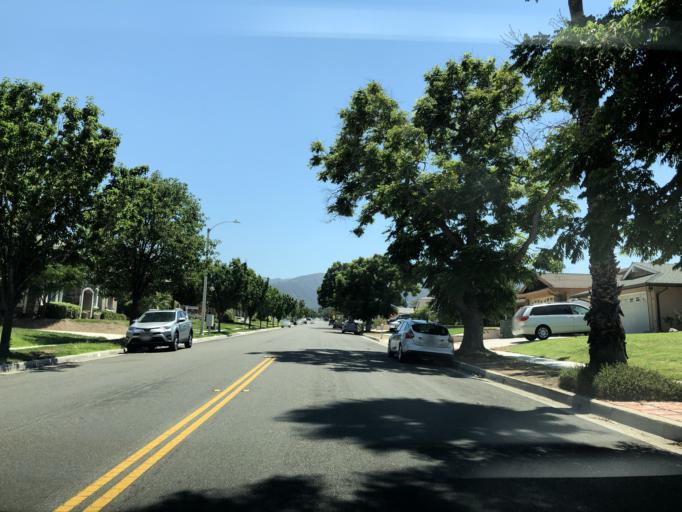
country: US
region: California
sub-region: Riverside County
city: Corona
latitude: 33.8541
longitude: -117.5754
